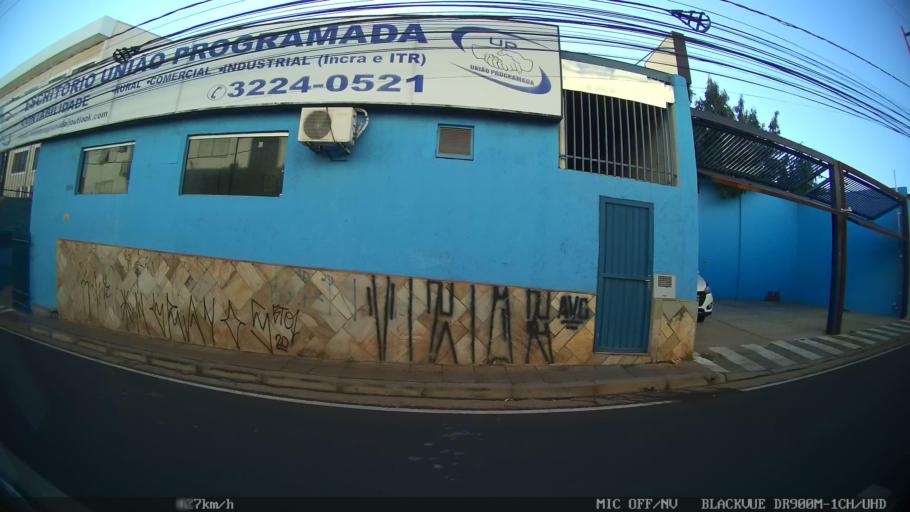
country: BR
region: Sao Paulo
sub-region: Sao Jose Do Rio Preto
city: Sao Jose do Rio Preto
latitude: -20.8050
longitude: -49.3754
